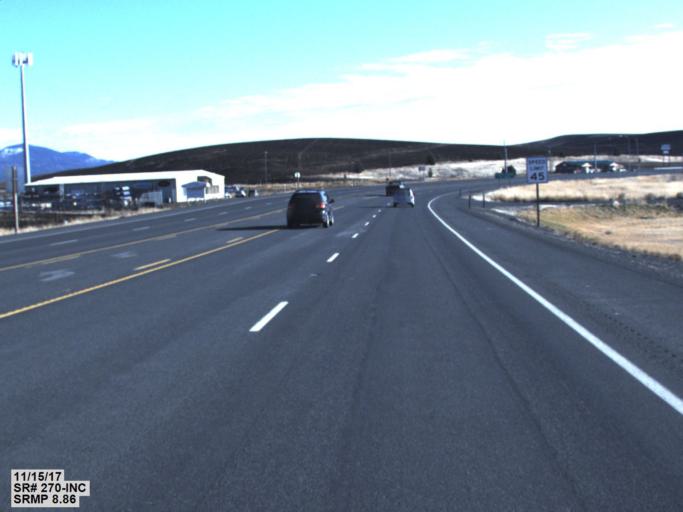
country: US
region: Idaho
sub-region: Latah County
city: Moscow
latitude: 46.7390
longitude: -117.0584
